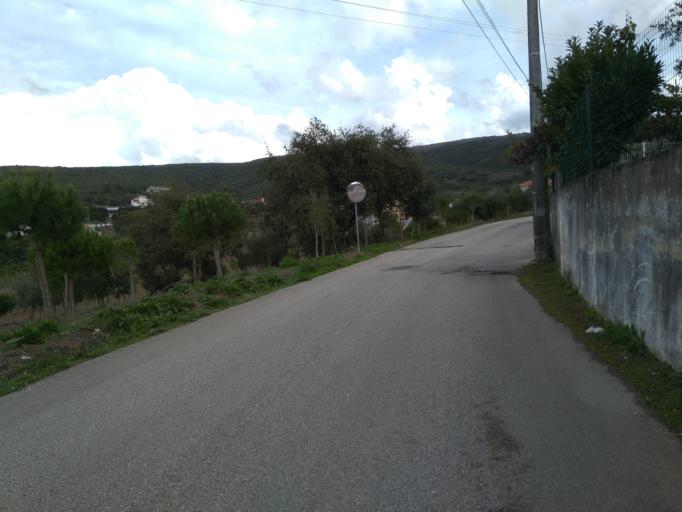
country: PT
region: Leiria
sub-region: Porto de Mos
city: Porto de Mos
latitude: 39.5982
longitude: -8.8101
